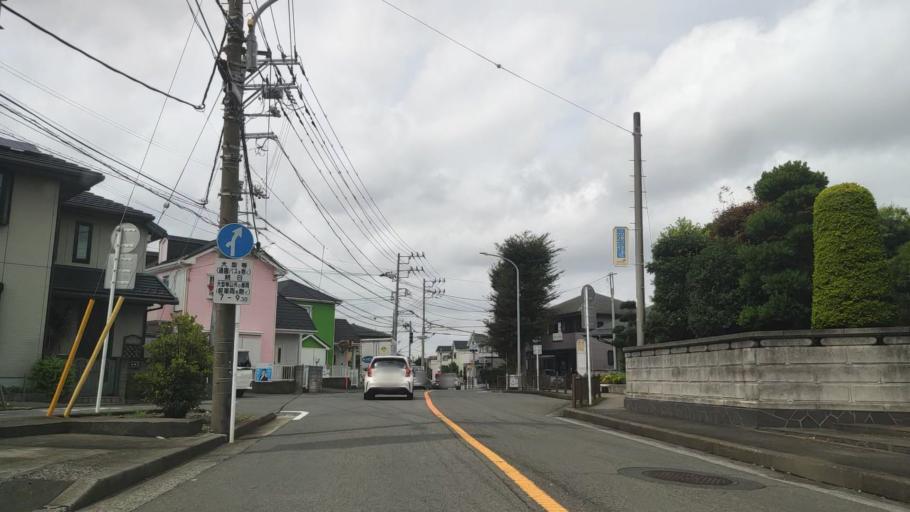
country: JP
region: Kanagawa
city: Minami-rinkan
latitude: 35.4720
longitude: 139.4892
